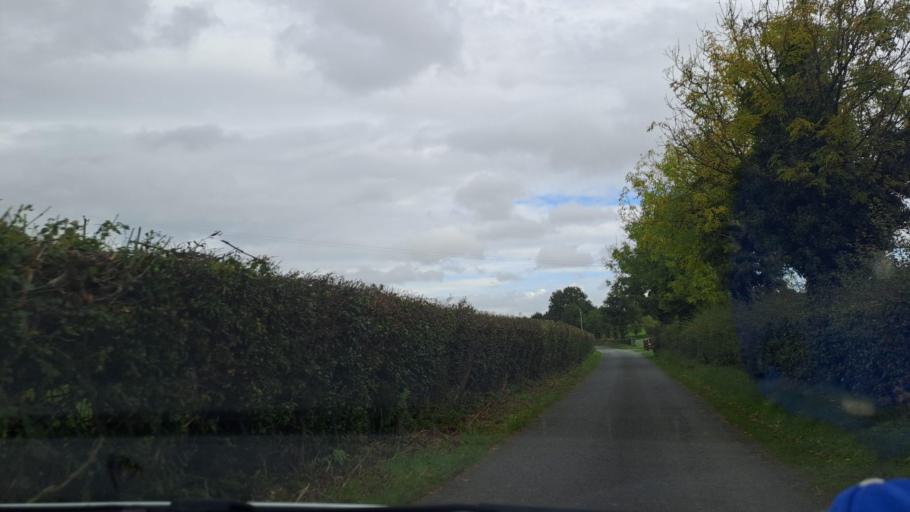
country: IE
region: Ulster
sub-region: An Cabhan
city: Kingscourt
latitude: 53.9395
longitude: -6.8114
